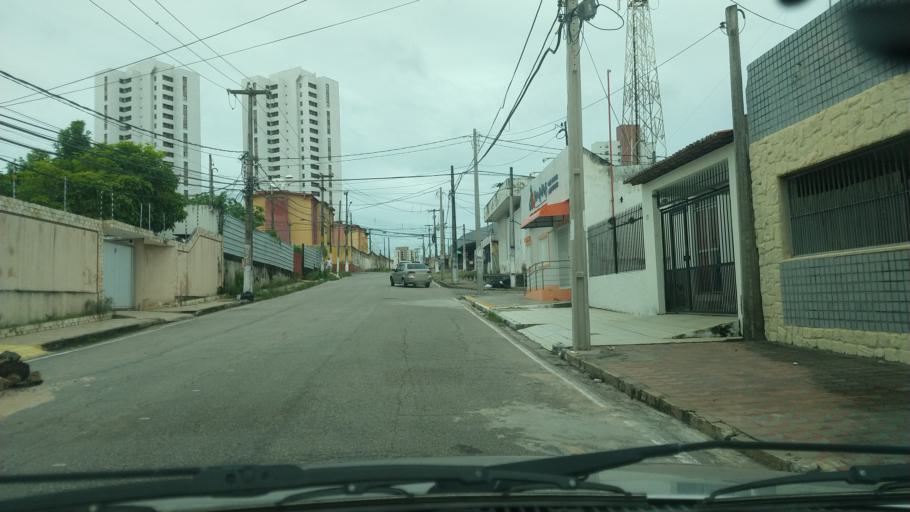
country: BR
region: Rio Grande do Norte
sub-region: Natal
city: Natal
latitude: -5.8553
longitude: -35.2065
